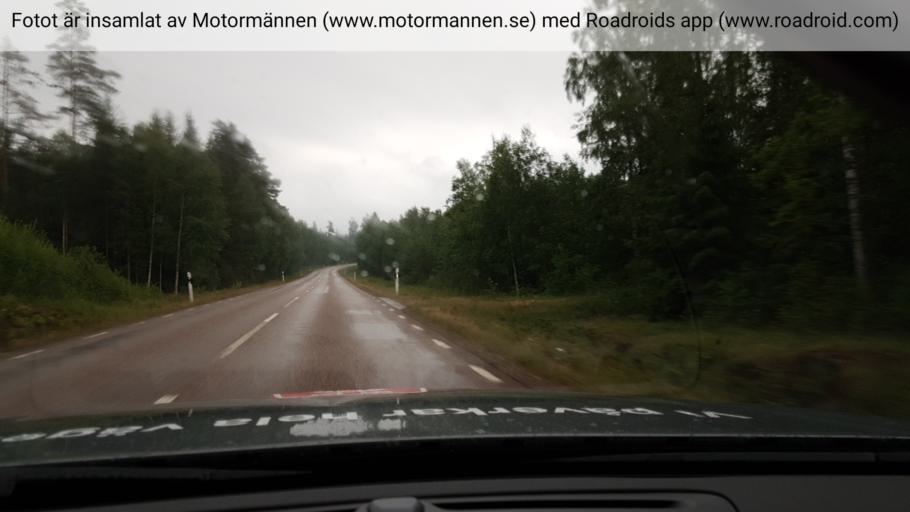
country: SE
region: Vaestmanland
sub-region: Norbergs Kommun
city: Norberg
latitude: 60.0081
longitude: 16.0642
